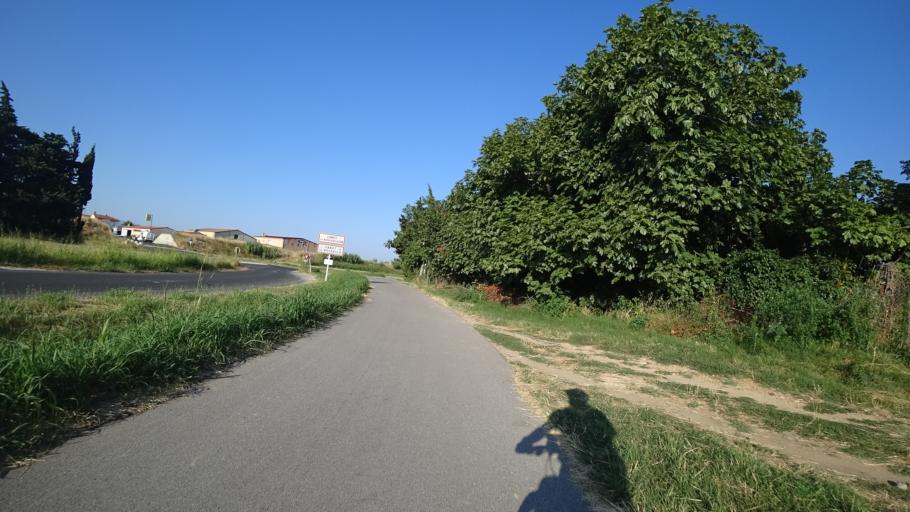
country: FR
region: Languedoc-Roussillon
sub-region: Departement des Pyrenees-Orientales
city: Canet-en-Roussillon
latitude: 42.7091
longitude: 3.0194
